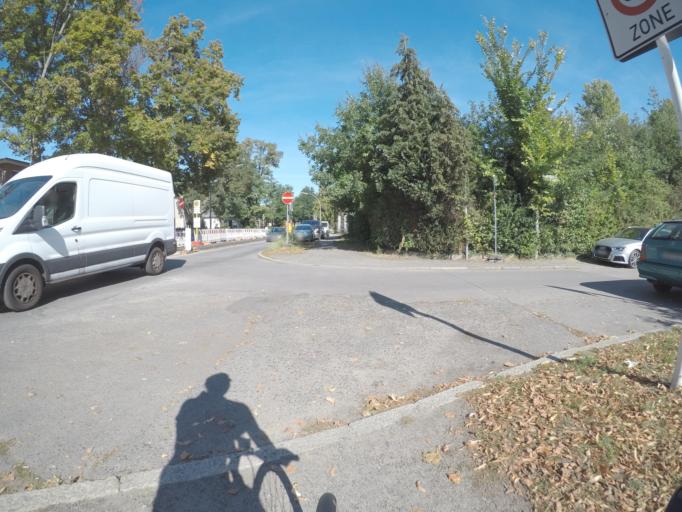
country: DE
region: Berlin
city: Heiligensee
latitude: 52.6168
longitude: 13.2206
